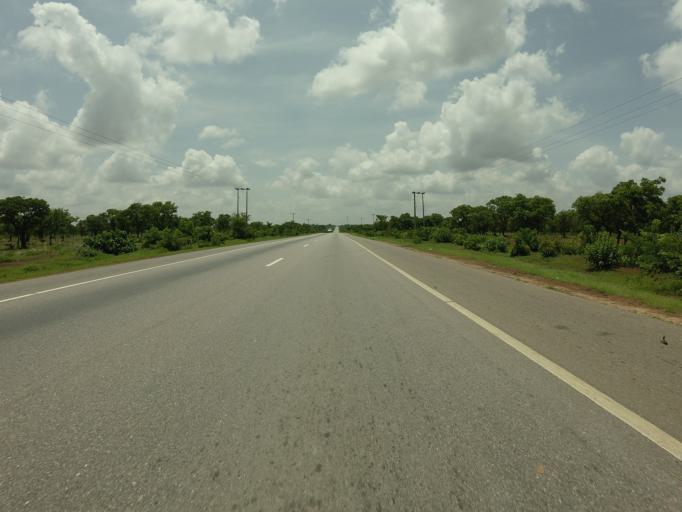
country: GH
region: Northern
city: Tamale
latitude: 9.2418
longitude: -1.0328
